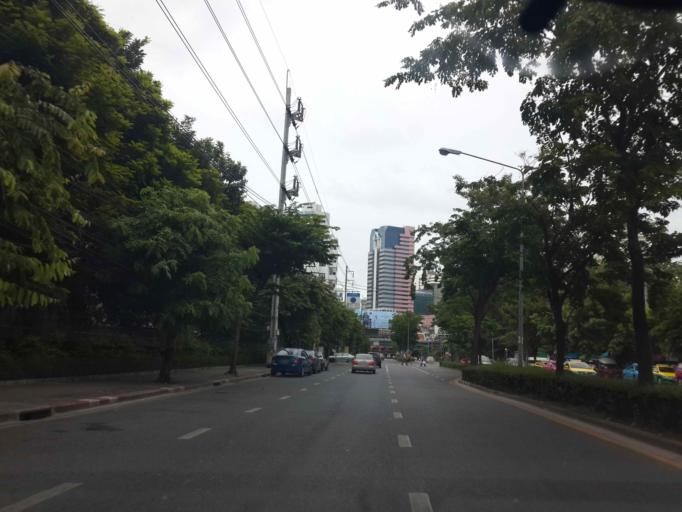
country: TH
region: Bangkok
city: Pathum Wan
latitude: 13.7340
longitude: 100.5341
